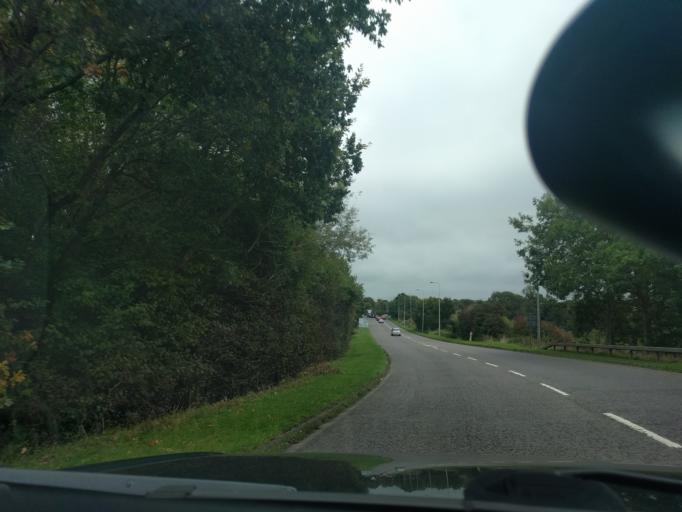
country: GB
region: England
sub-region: Wiltshire
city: Chippenham
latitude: 51.4529
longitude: -2.1163
